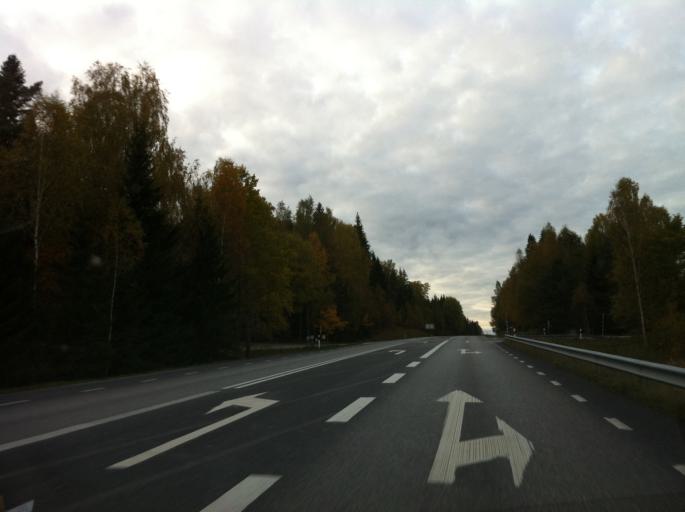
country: SE
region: OErebro
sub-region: Nora Kommun
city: Nora
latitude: 59.4809
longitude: 15.0859
